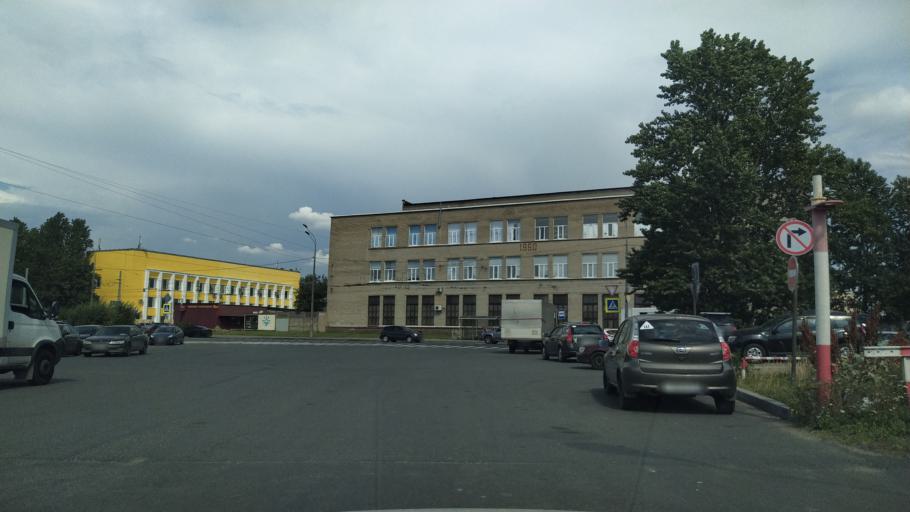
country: RU
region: Leningrad
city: Finlyandskiy
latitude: 59.9653
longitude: 30.3663
